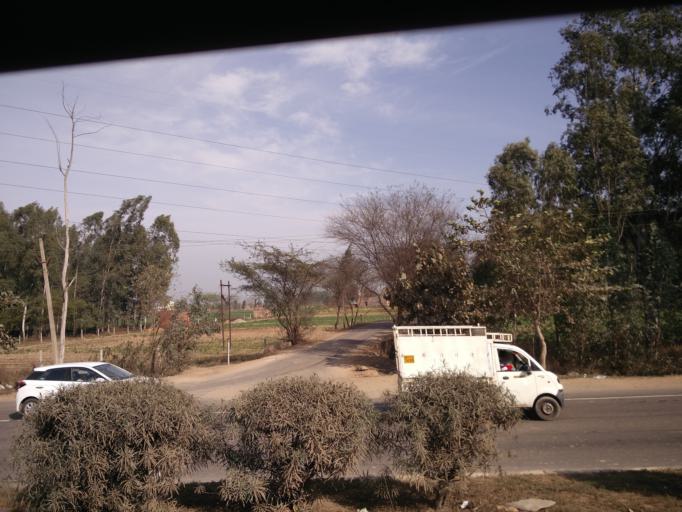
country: IN
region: Haryana
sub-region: Ambala
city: Ambala
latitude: 30.4078
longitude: 76.7855
